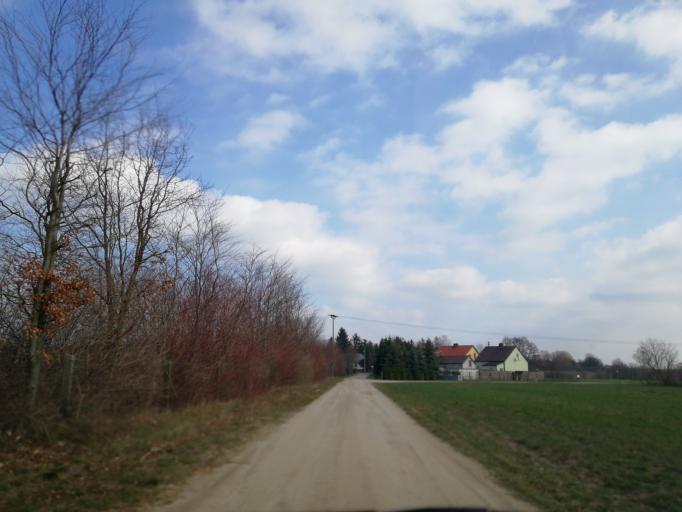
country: DE
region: Brandenburg
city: Finsterwalde
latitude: 51.6625
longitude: 13.7349
